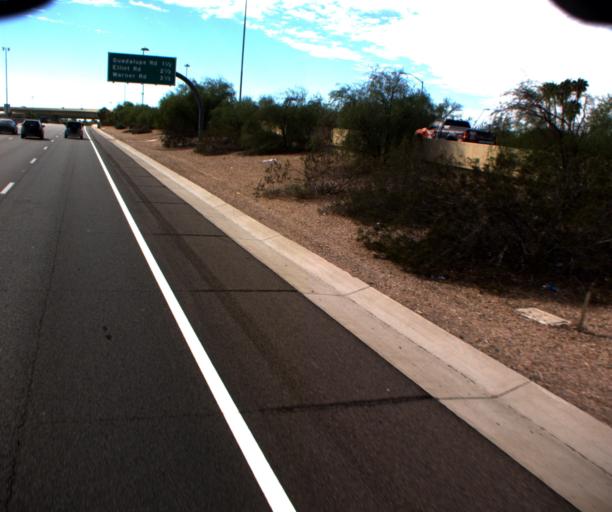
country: US
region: Arizona
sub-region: Maricopa County
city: Tempe
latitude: 33.3902
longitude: -111.8913
